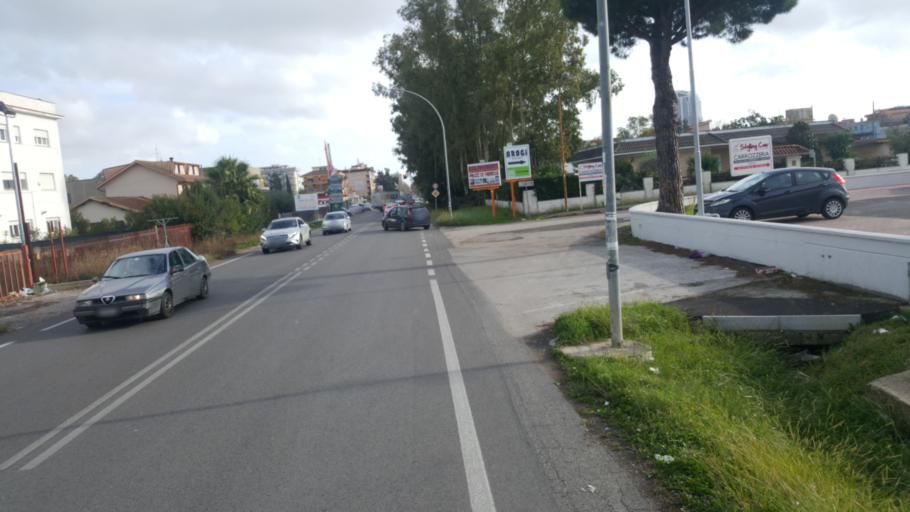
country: IT
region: Latium
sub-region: Provincia di Latina
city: Latina
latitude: 41.4747
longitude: 12.8835
